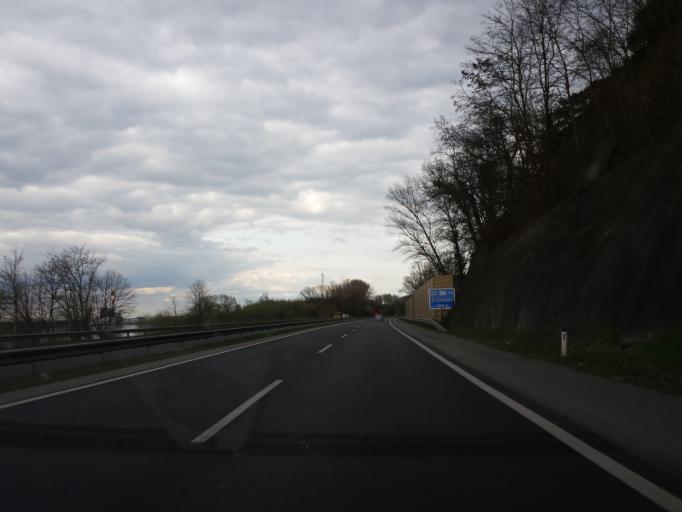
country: AT
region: Lower Austria
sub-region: Politischer Bezirk Krems
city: Gedersdorf
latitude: 48.3801
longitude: 15.6805
